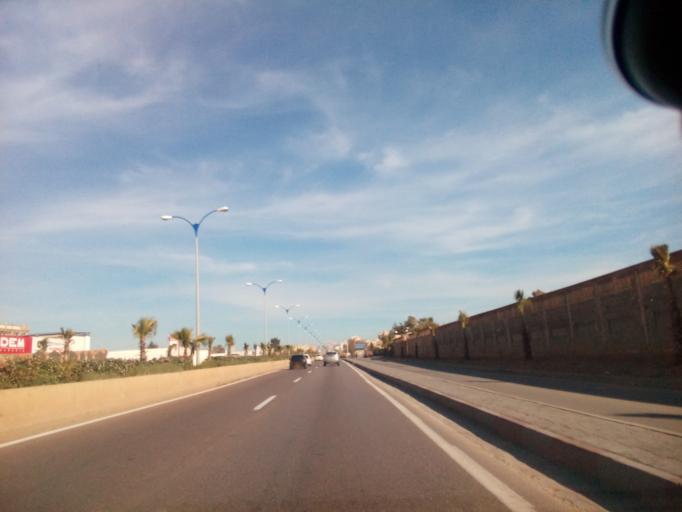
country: DZ
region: Mostaganem
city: Mostaganem
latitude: 35.9123
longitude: 0.0723
